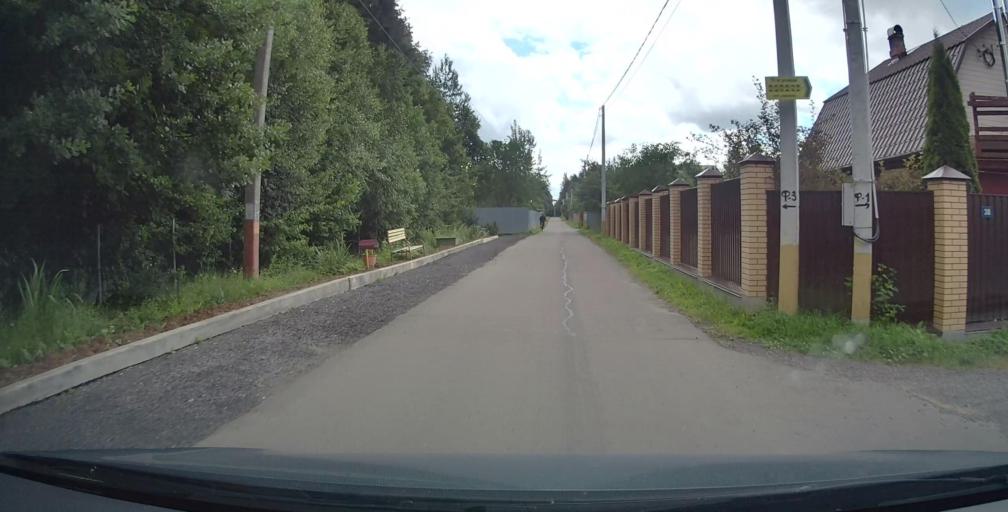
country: RU
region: Moskovskaya
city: Selyatino
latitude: 55.3935
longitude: 37.0171
